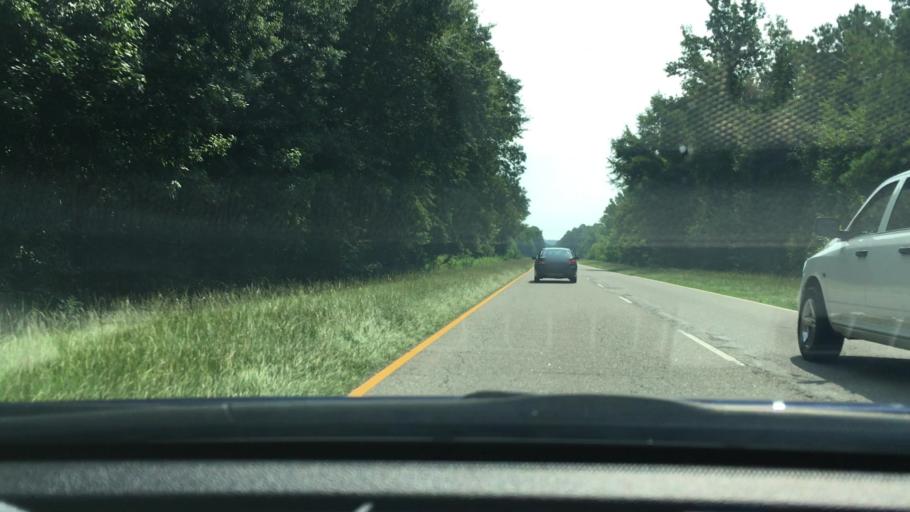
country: US
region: South Carolina
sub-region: Sumter County
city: Stateburg
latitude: 33.9513
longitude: -80.5827
